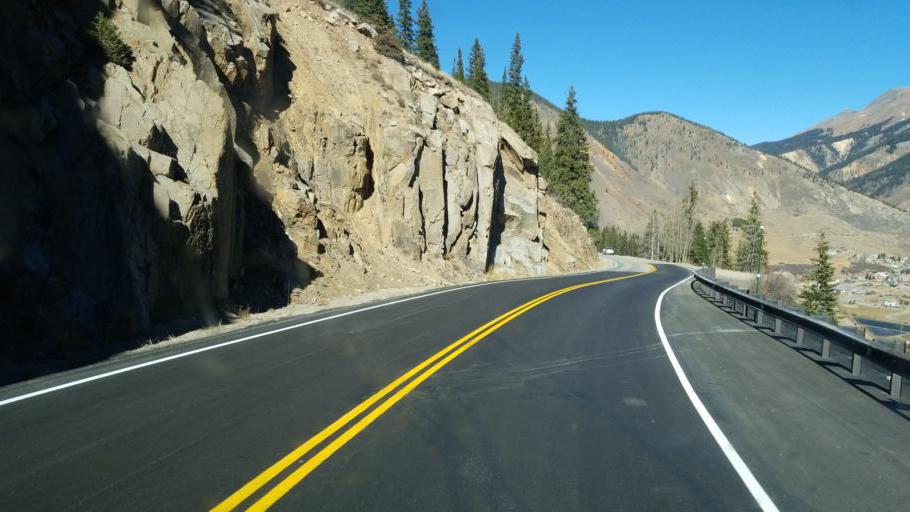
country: US
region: Colorado
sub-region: San Juan County
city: Silverton
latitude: 37.7935
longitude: -107.6734
